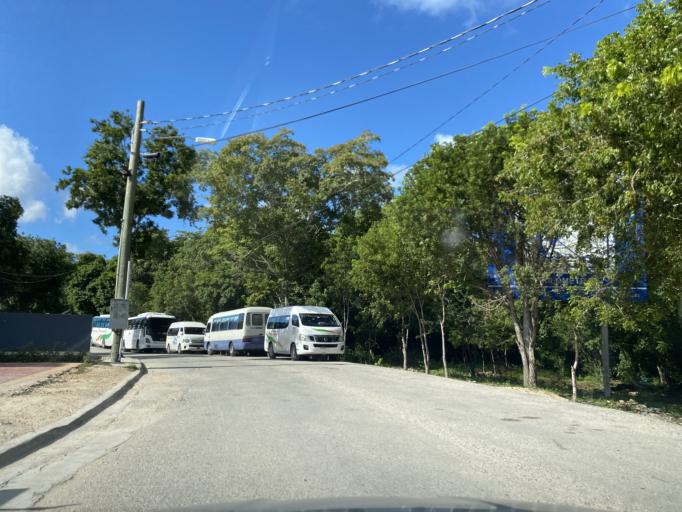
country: DO
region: La Romana
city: La Romana
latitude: 18.3700
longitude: -68.8389
